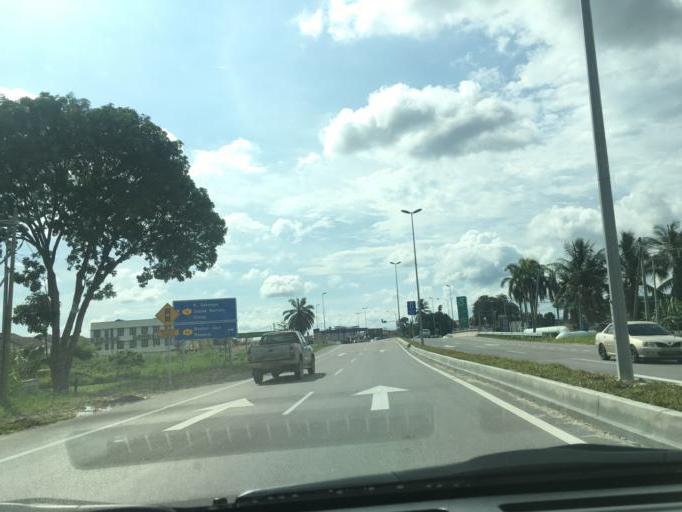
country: MY
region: Selangor
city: Batu Arang
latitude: 3.3133
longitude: 101.4182
